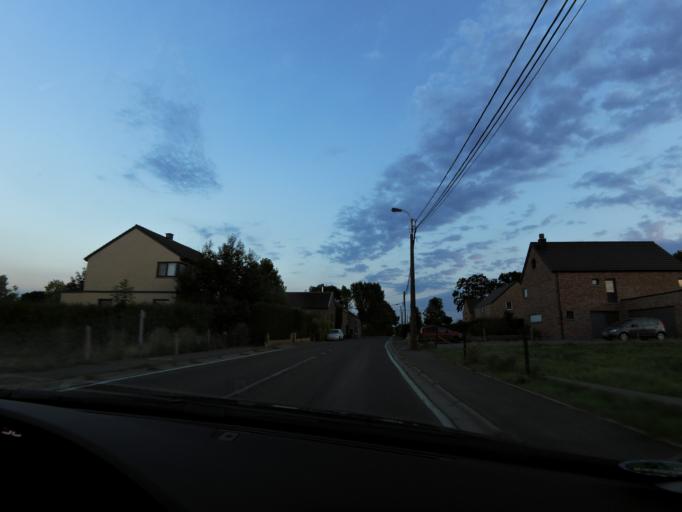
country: BE
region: Wallonia
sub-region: Province de Liege
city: La Calamine
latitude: 50.7107
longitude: 5.9852
